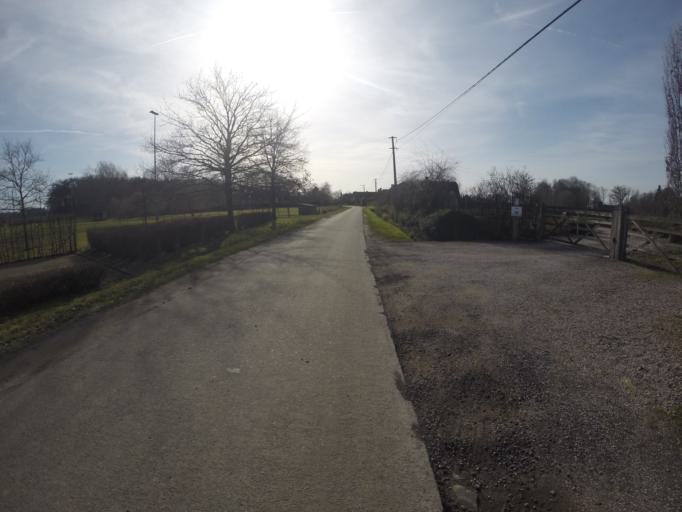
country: BE
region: Flanders
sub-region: Provincie West-Vlaanderen
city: Oostkamp
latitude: 51.1102
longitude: 3.2602
